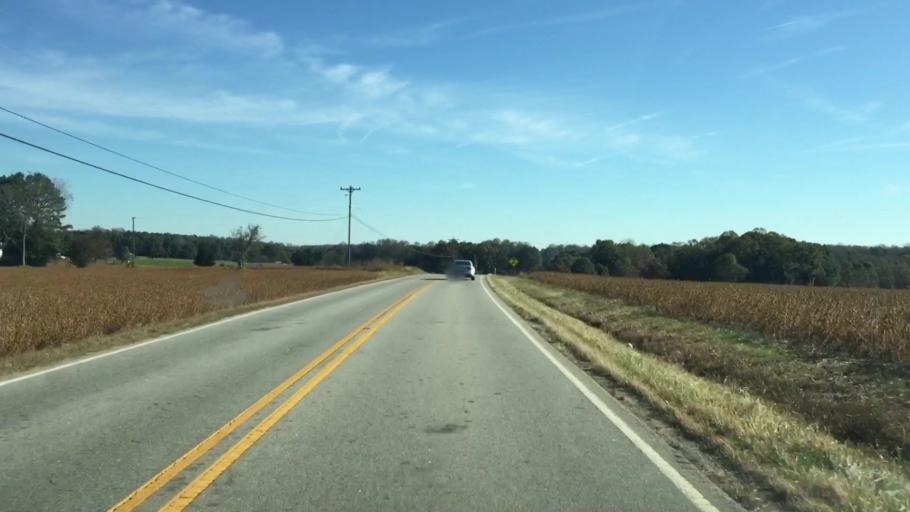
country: US
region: North Carolina
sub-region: Rowan County
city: China Grove
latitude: 35.6391
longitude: -80.6615
